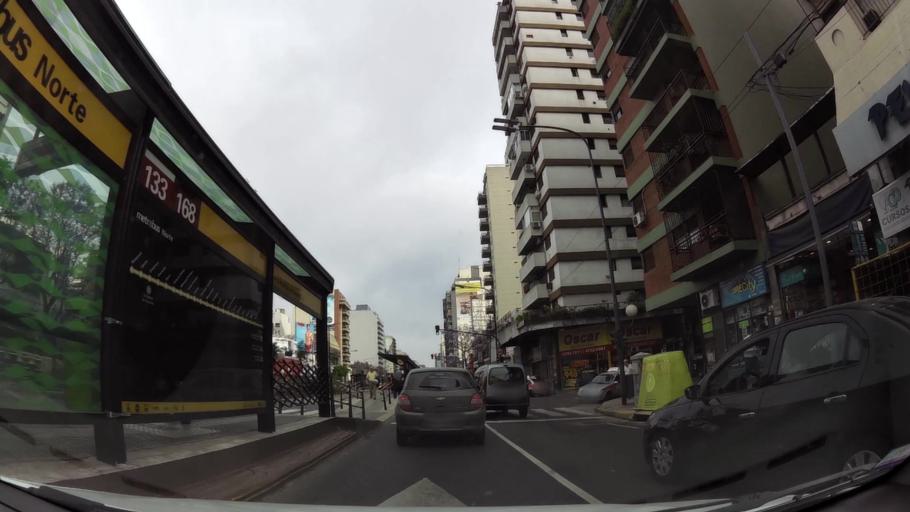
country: AR
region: Buenos Aires F.D.
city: Colegiales
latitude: -34.5521
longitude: -58.4655
